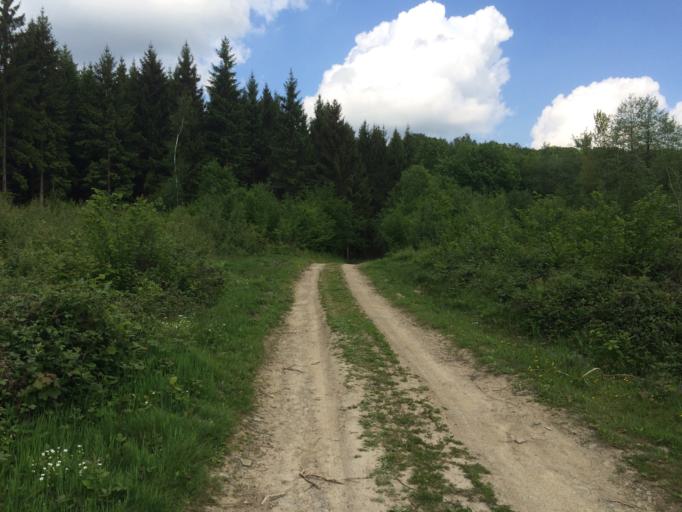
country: BE
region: Wallonia
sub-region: Province de Namur
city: Yvoir
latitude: 50.3303
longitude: 4.9493
